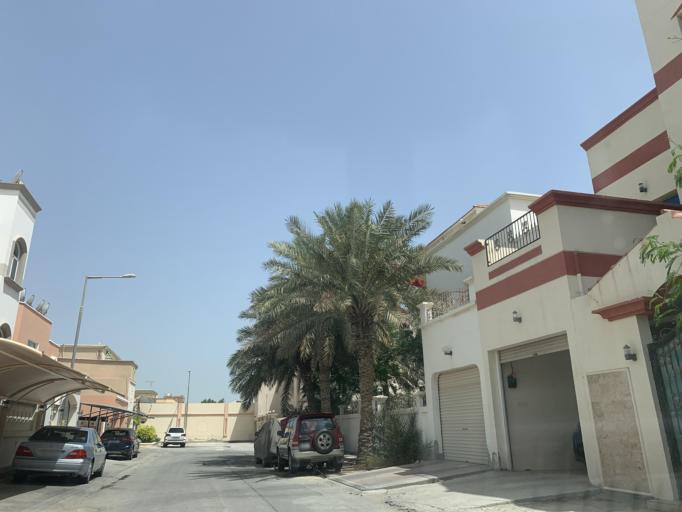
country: BH
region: Northern
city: Ar Rifa'
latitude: 26.1541
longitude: 50.5808
